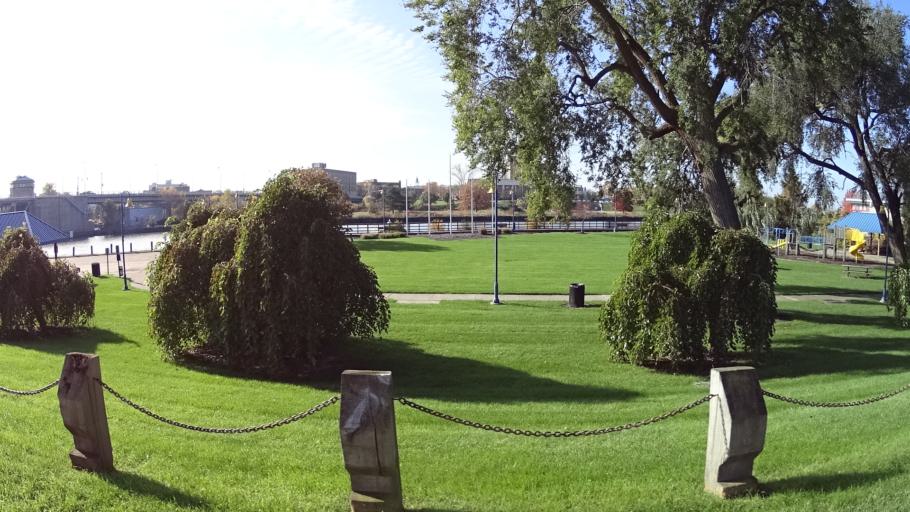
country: US
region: Ohio
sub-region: Lorain County
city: Lorain
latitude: 41.4710
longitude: -82.1765
